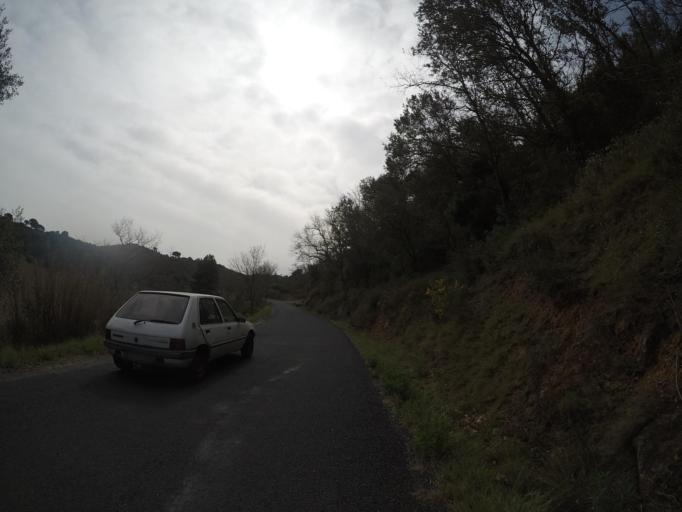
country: FR
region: Languedoc-Roussillon
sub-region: Departement des Pyrenees-Orientales
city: Estagel
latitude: 42.7496
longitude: 2.7226
